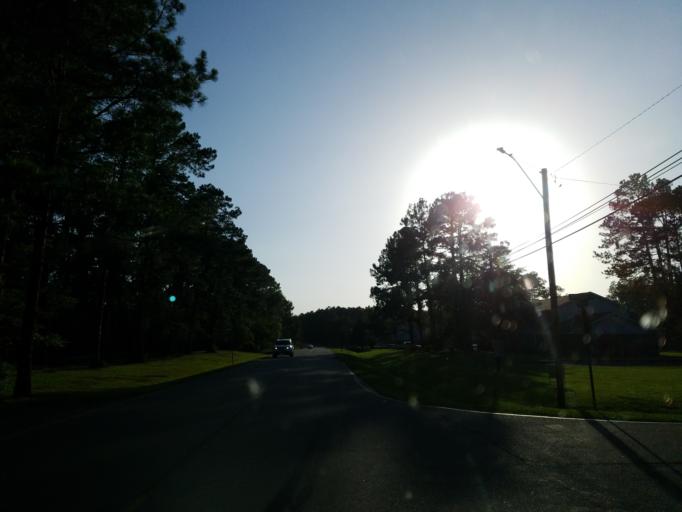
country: US
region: Georgia
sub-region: Ben Hill County
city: Fitzgerald
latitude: 31.7142
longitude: -83.2811
